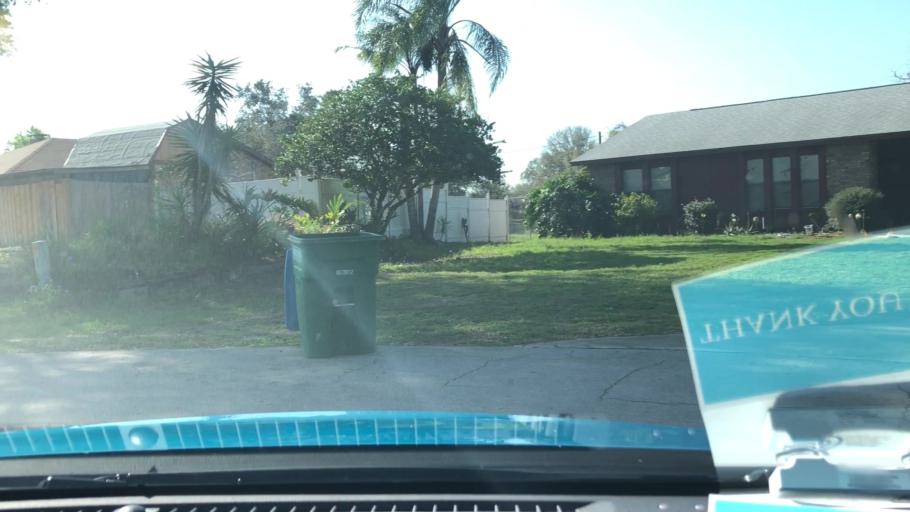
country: US
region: Florida
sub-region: Volusia County
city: Deltona
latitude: 28.9147
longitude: -81.2580
